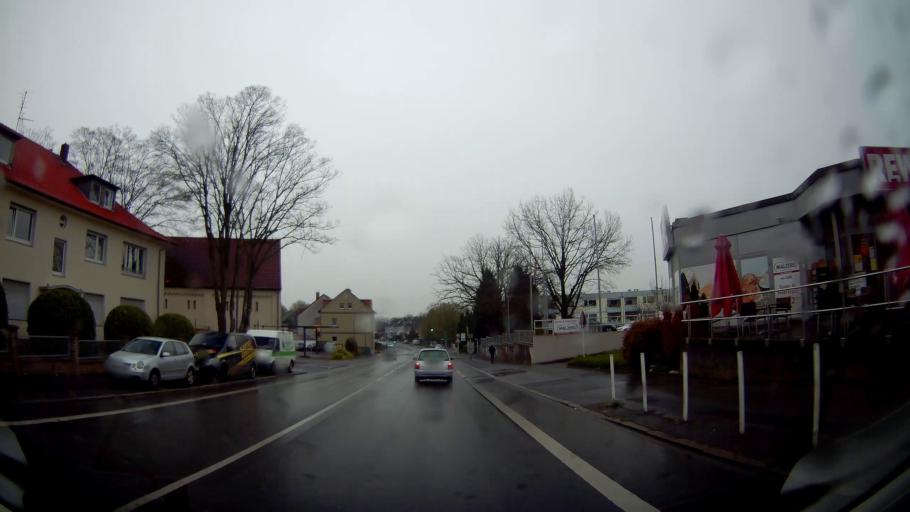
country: DE
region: North Rhine-Westphalia
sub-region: Regierungsbezirk Arnsberg
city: Dortmund
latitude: 51.5246
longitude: 7.3872
